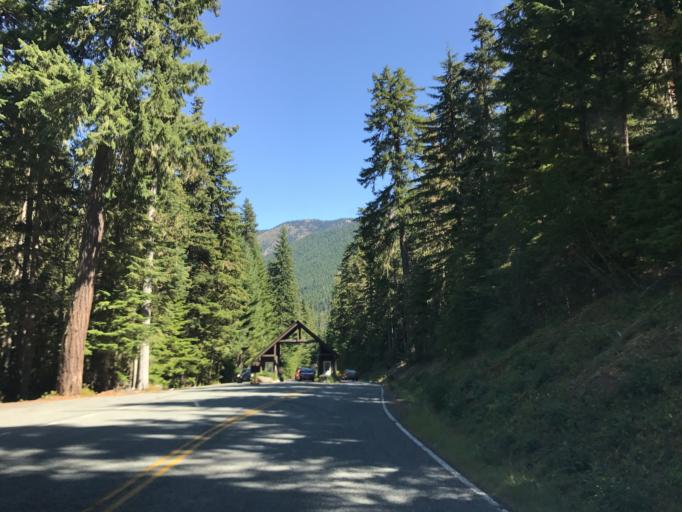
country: US
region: Washington
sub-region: King County
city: Enumclaw
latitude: 46.9017
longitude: -121.5543
